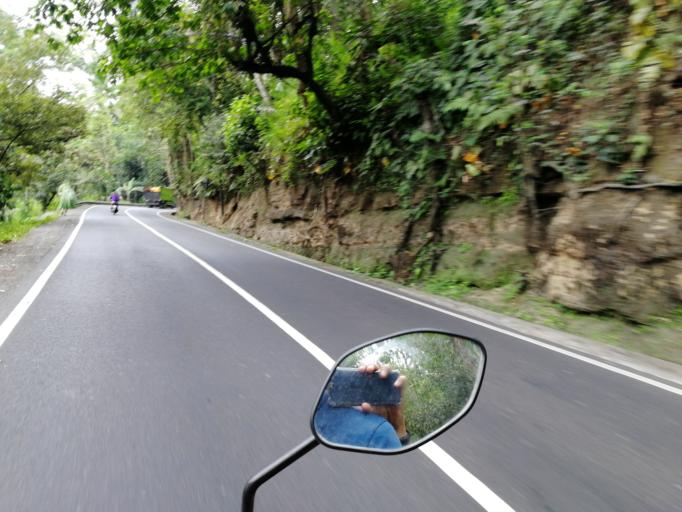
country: ID
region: Bali
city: Banjar Geriana Kangin
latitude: -8.4267
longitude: 115.4363
